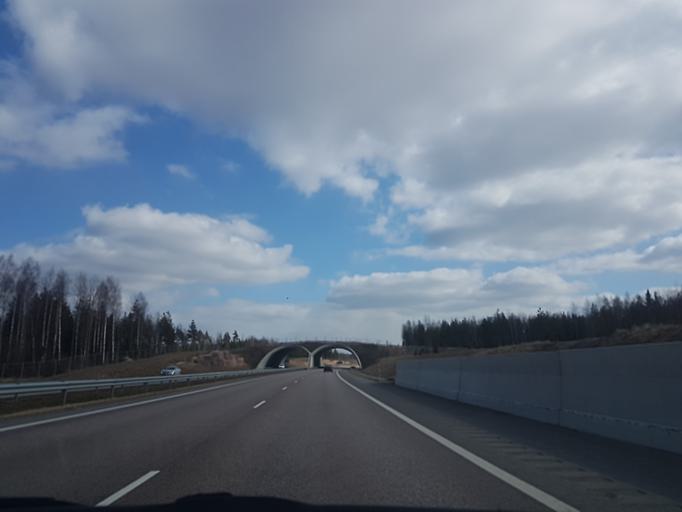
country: FI
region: Kymenlaakso
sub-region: Kotka-Hamina
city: Broby
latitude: 60.5032
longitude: 26.8015
